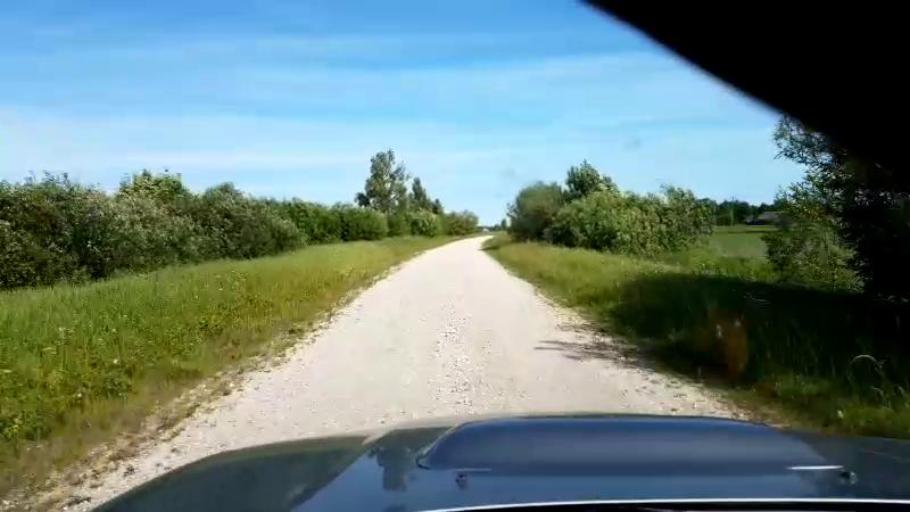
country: EE
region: Paernumaa
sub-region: Sauga vald
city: Sauga
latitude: 58.4722
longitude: 24.5329
